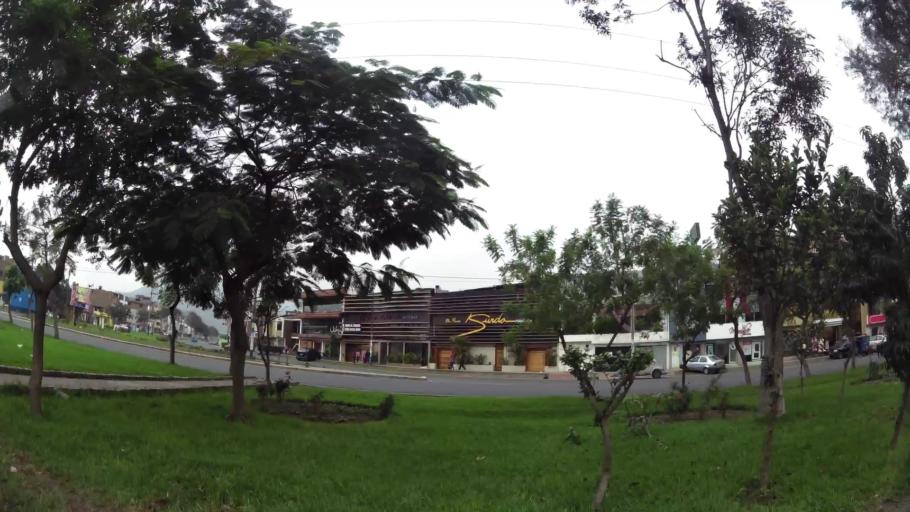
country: PE
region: Lima
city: Lima
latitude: -12.0086
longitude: -77.0111
